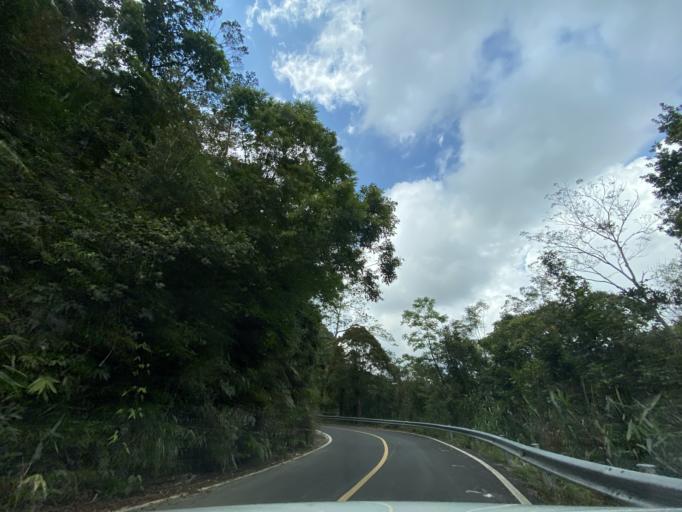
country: CN
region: Hainan
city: Diaoluoshan
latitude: 18.7002
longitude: 109.8832
